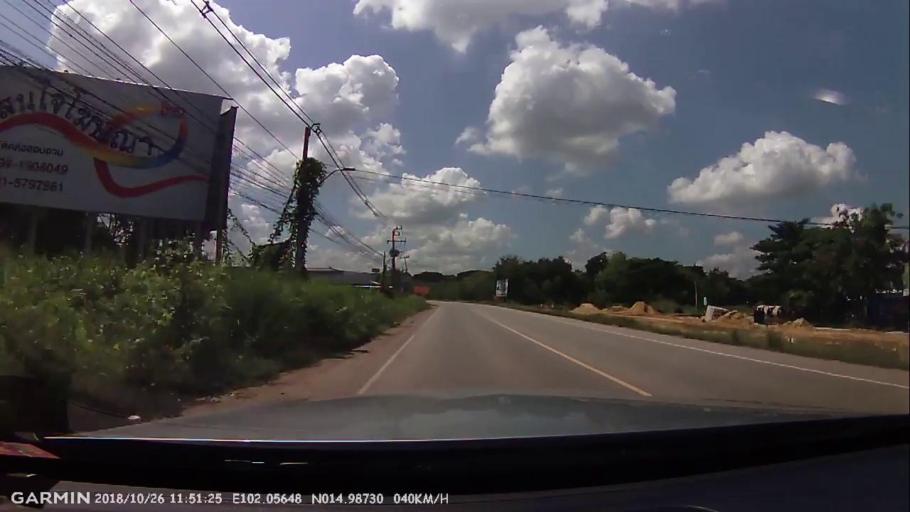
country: TH
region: Nakhon Ratchasima
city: Nakhon Ratchasima
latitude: 14.9868
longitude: 102.0565
